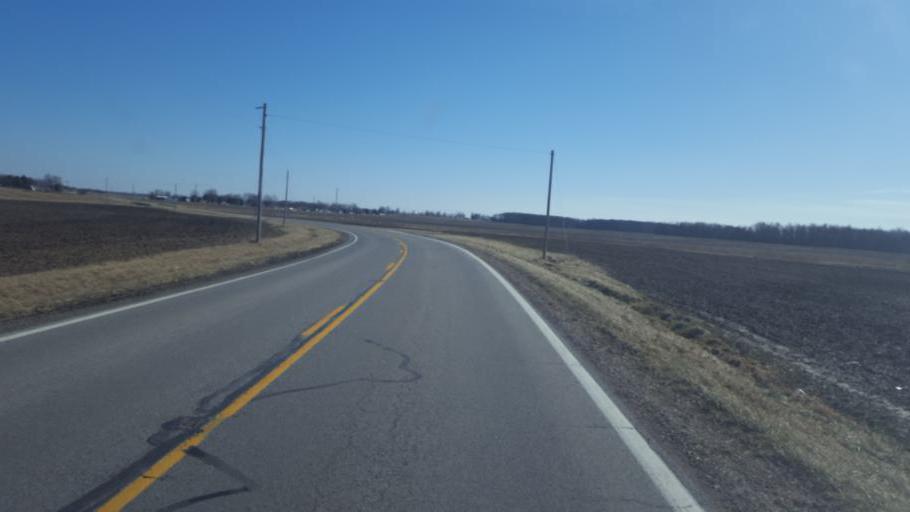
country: US
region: Ohio
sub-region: Marion County
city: Marion
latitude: 40.6250
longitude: -83.2545
